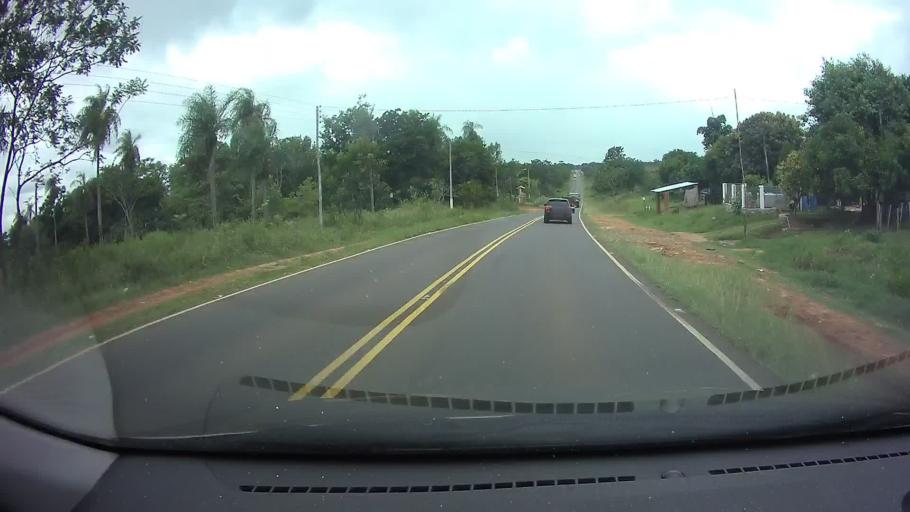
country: PY
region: Paraguari
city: Carapegua
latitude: -25.7460
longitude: -57.2710
